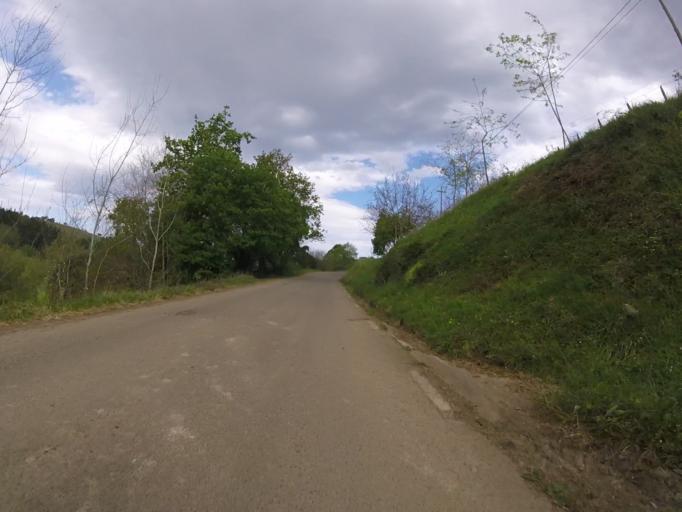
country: ES
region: Basque Country
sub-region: Provincia de Guipuzcoa
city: Zarautz
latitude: 43.2613
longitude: -2.1681
